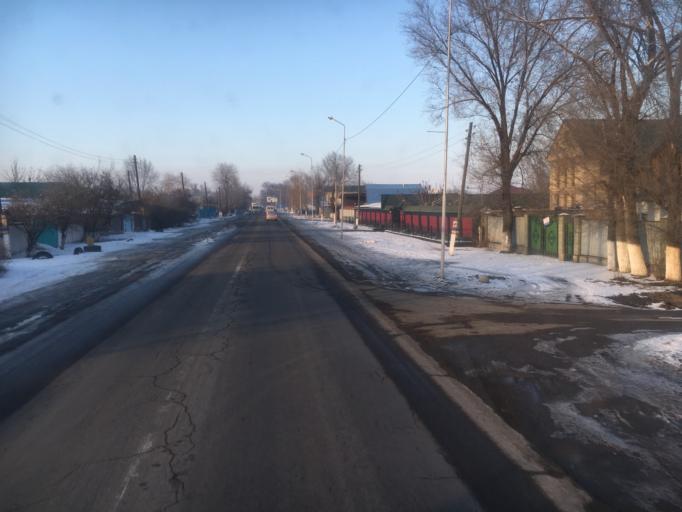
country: KZ
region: Almaty Oblysy
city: Burunday
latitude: 43.3719
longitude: 76.6416
